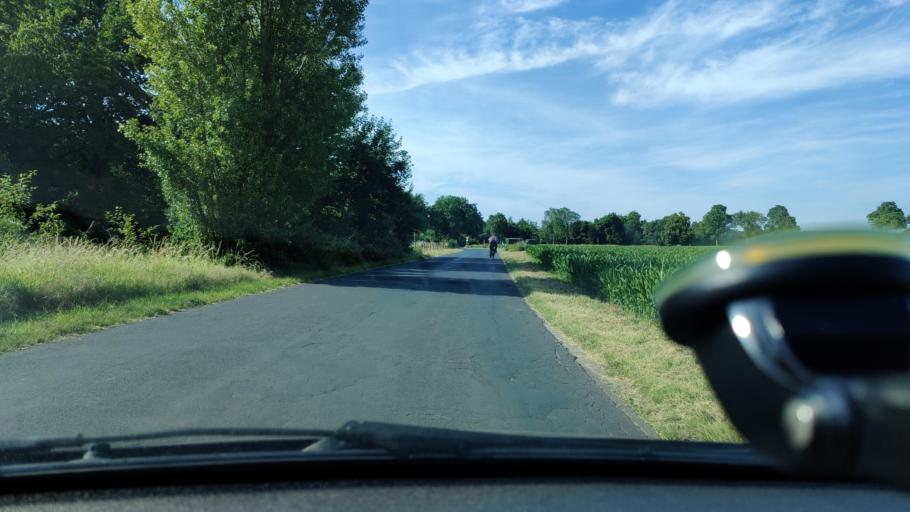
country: DE
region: North Rhine-Westphalia
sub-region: Regierungsbezirk Dusseldorf
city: Rheurdt
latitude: 51.5056
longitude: 6.4948
